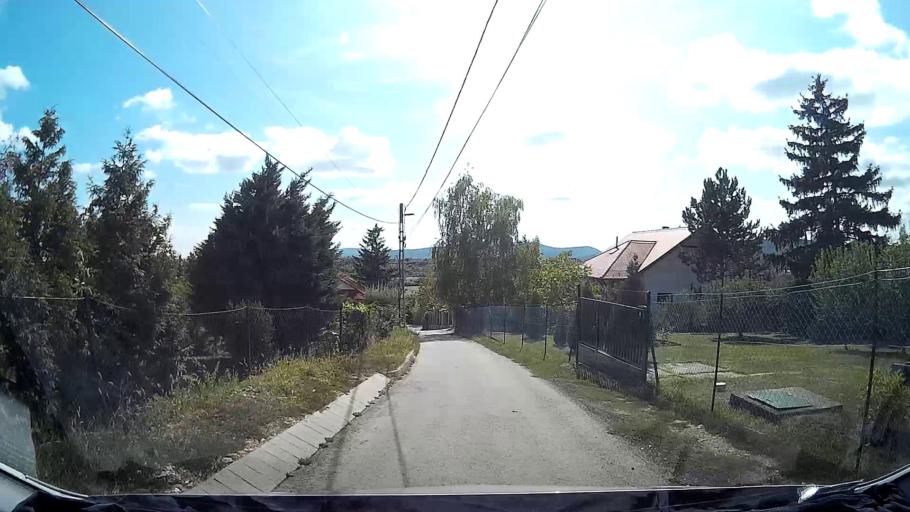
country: HU
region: Pest
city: Szentendre
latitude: 47.6890
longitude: 19.0630
